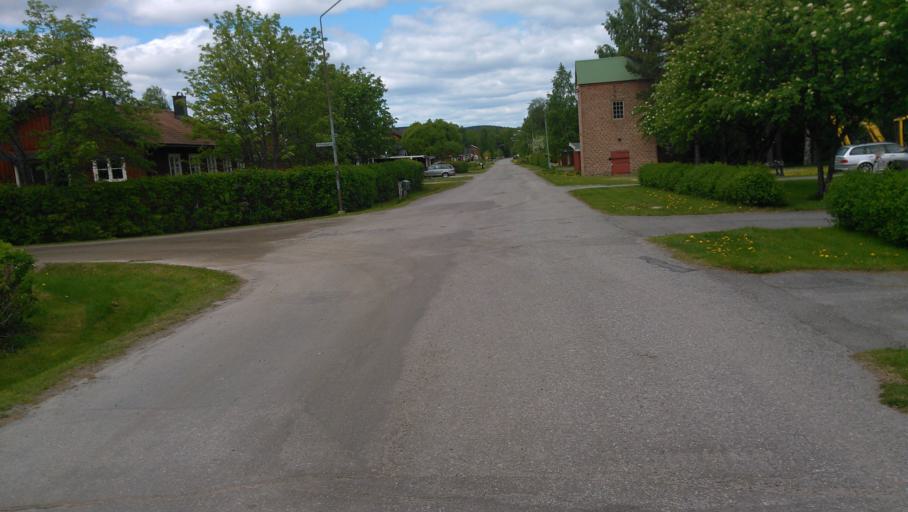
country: SE
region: Vaesterbotten
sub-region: Umea Kommun
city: Roback
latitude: 63.8753
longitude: 20.0578
